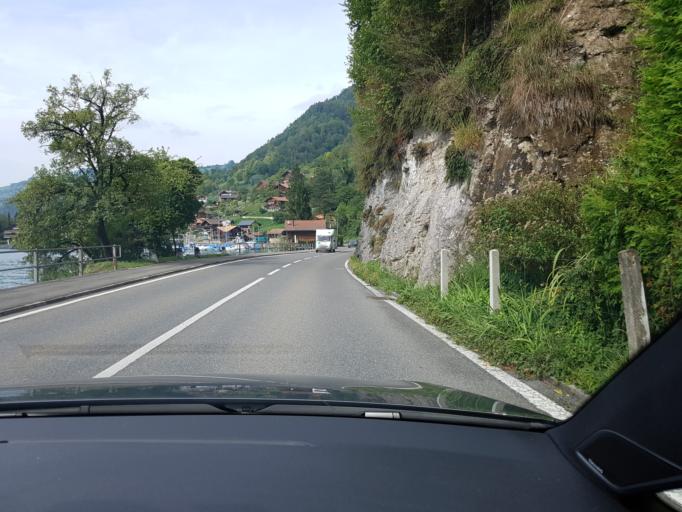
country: CH
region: Bern
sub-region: Thun District
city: Sigriswil
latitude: 46.6921
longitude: 7.7435
